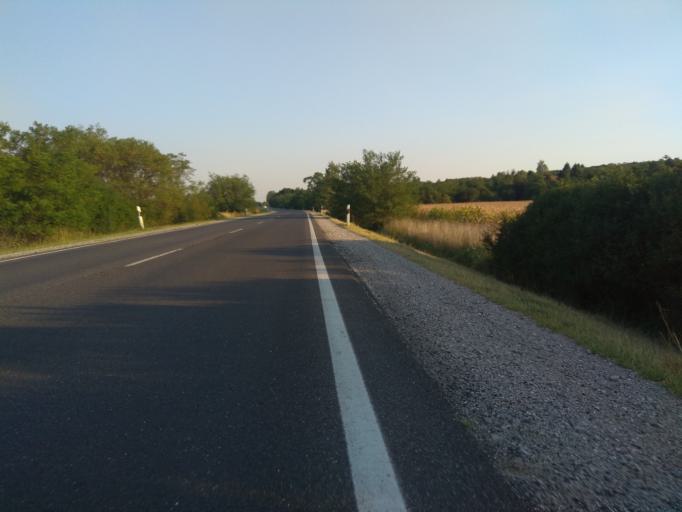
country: HU
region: Borsod-Abauj-Zemplen
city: Nyekladhaza
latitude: 47.9709
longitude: 20.8310
